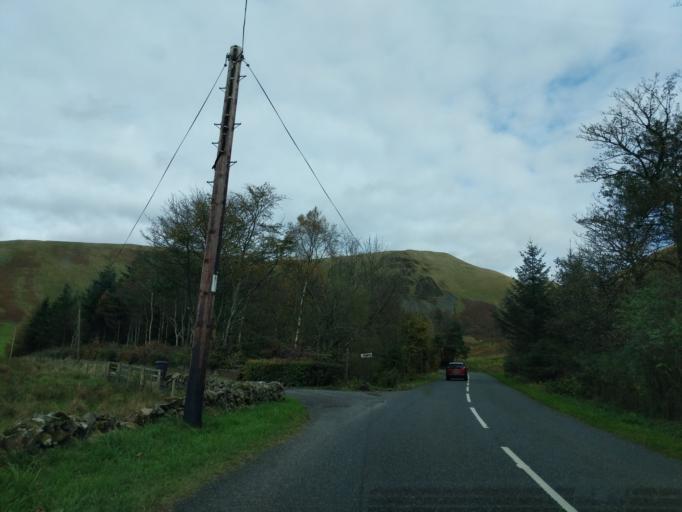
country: GB
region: Scotland
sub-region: Dumfries and Galloway
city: Thornhill
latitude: 55.3398
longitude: -3.7582
